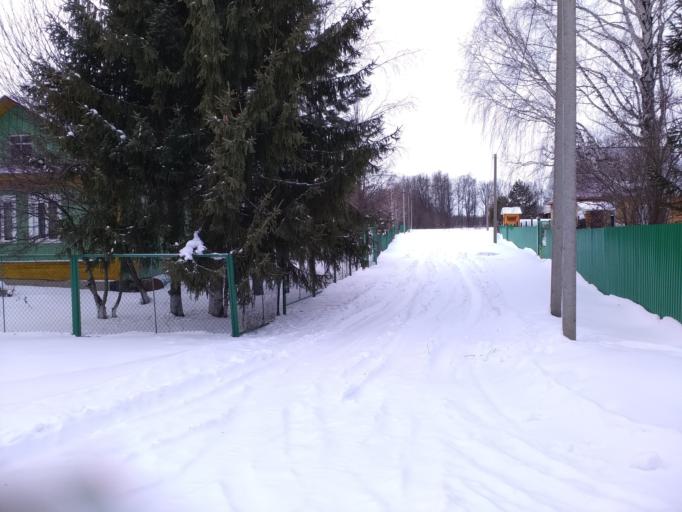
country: RU
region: Bashkortostan
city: Kudeyevskiy
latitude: 54.7145
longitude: 56.6914
